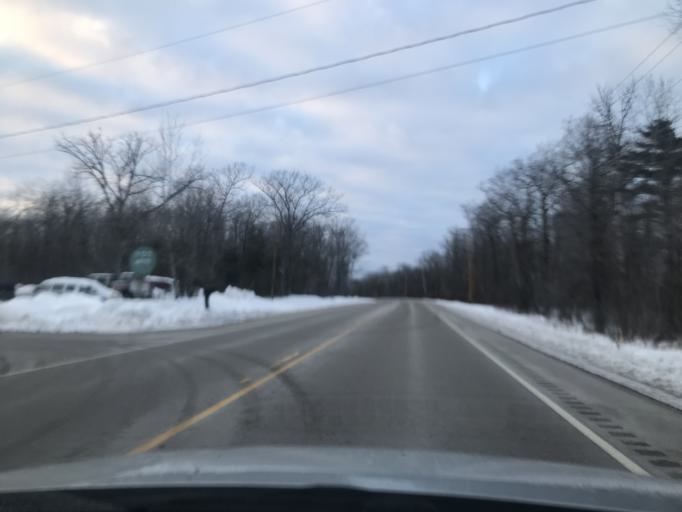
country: US
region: Wisconsin
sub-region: Marinette County
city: Marinette
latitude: 45.1517
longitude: -87.7056
